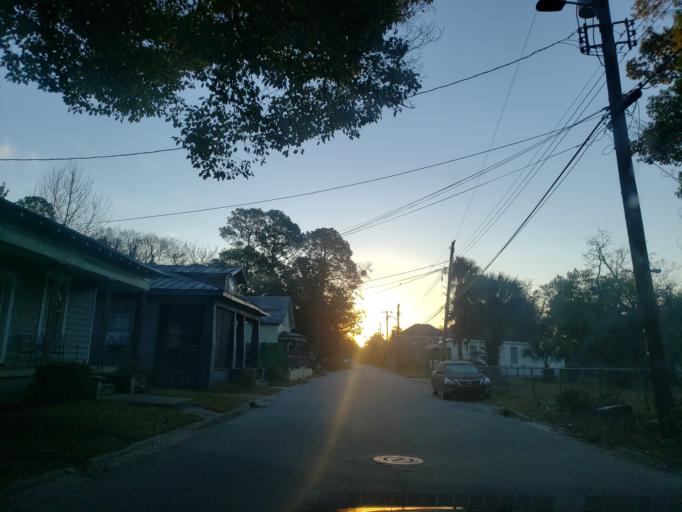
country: US
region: Georgia
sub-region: Chatham County
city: Savannah
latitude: 32.0441
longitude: -81.1075
